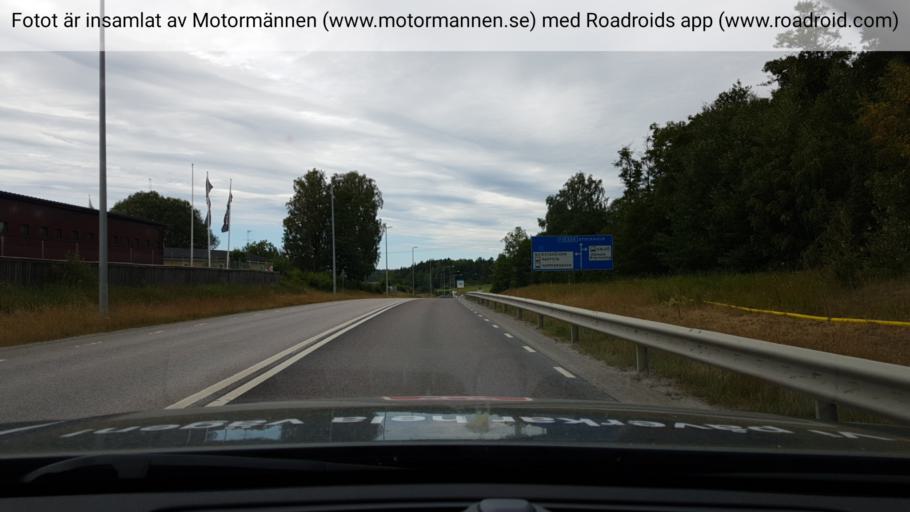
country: SE
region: Stockholm
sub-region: Nynashamns Kommun
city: Nynashamn
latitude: 58.9251
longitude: 17.9377
